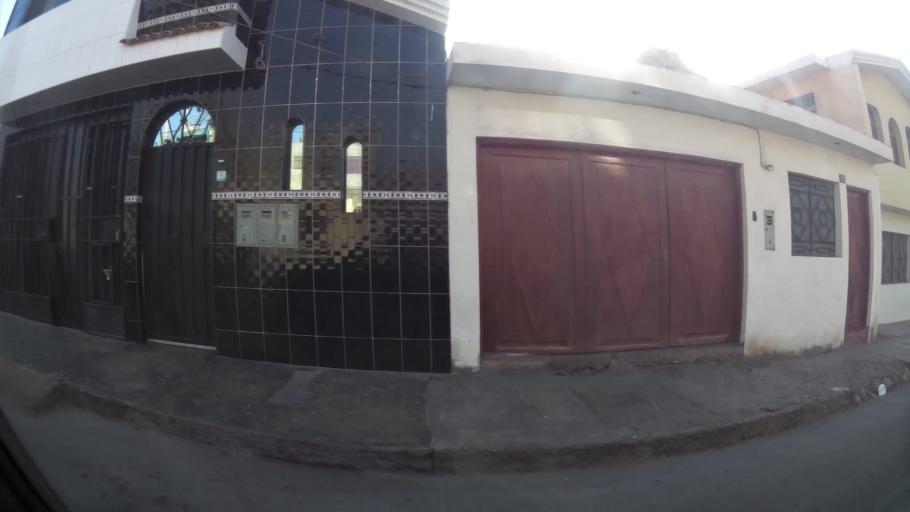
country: PE
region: Lima
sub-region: Huaura
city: Huacho
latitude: -11.1113
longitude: -77.6029
